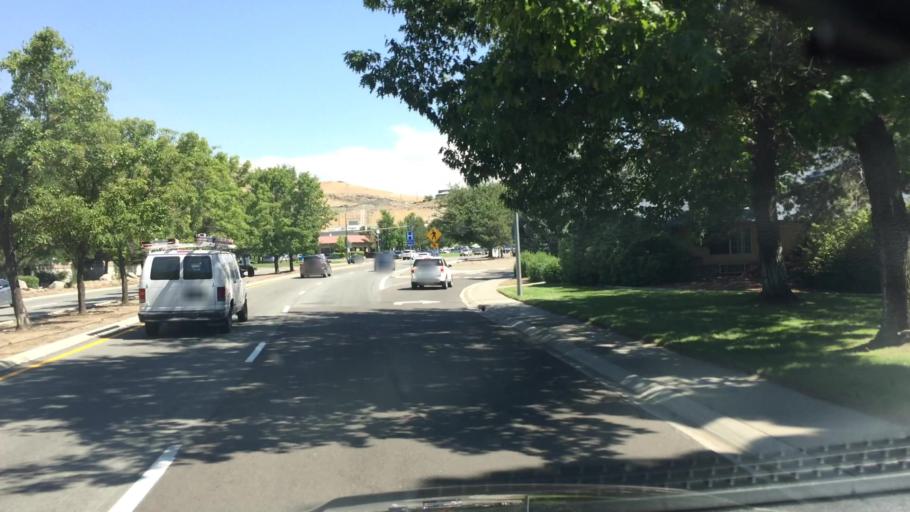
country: US
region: Nevada
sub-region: Washoe County
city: Sparks
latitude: 39.5432
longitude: -119.7048
